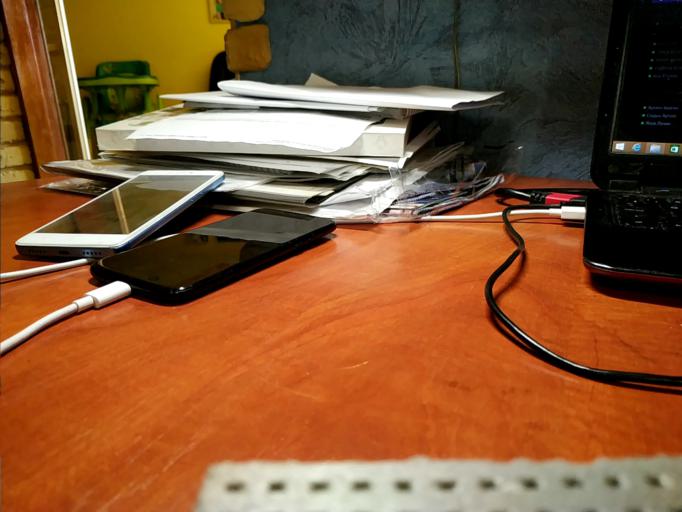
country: RU
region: Tverskaya
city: Kalashnikovo
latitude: 57.4111
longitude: 35.1652
